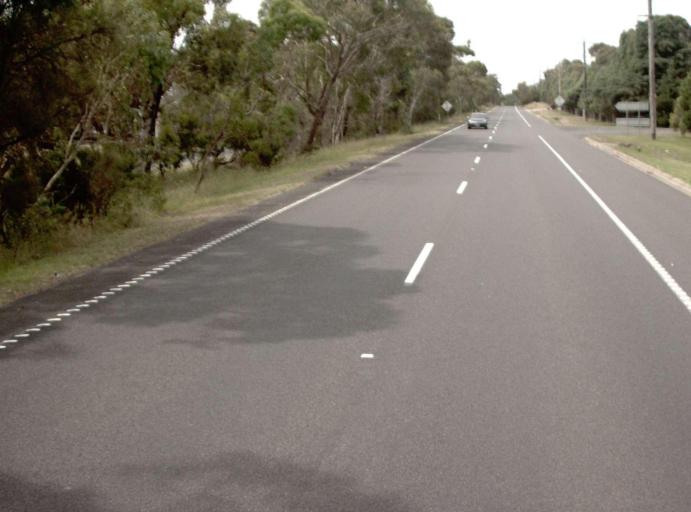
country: AU
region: Victoria
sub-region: Mornington Peninsula
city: Moorooduc
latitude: -38.2527
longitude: 145.0802
